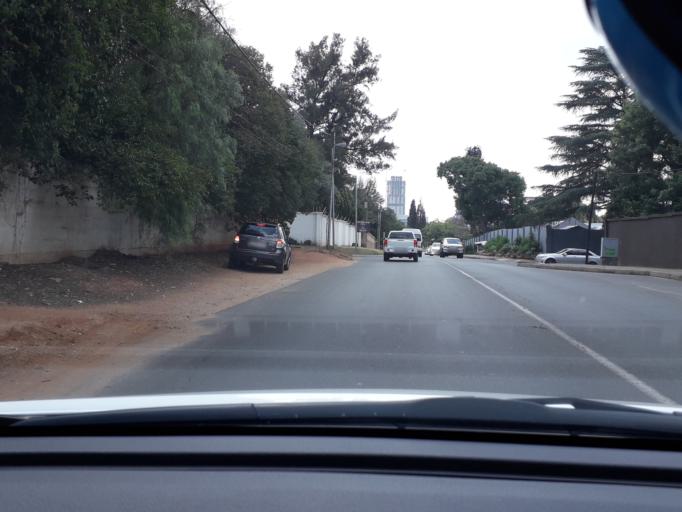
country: ZA
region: Gauteng
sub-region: City of Johannesburg Metropolitan Municipality
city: Johannesburg
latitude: -26.1236
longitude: 28.0633
